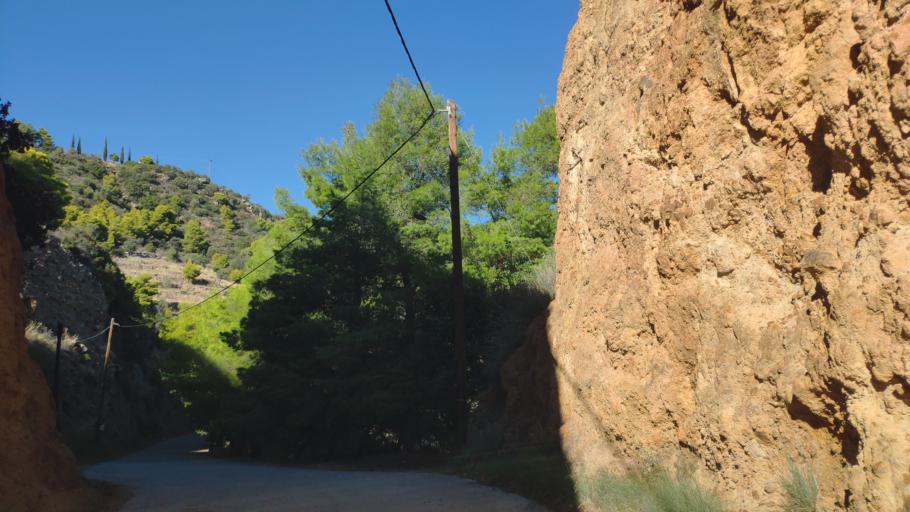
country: GR
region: Attica
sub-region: Nomos Piraios
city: Poros
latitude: 37.5894
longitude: 23.4020
